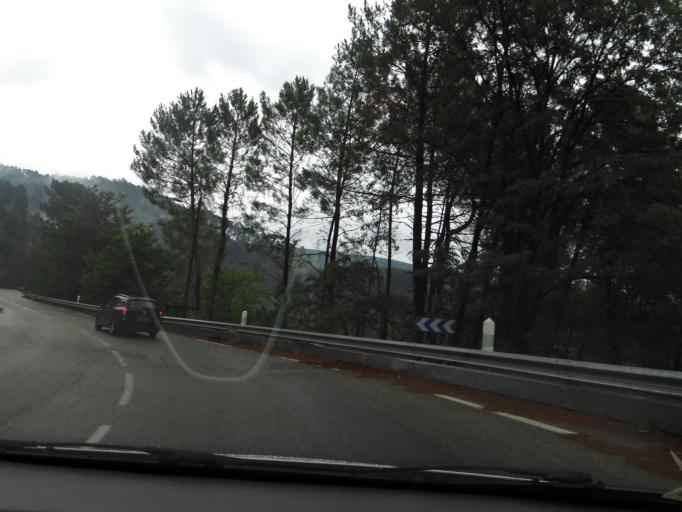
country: FR
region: Languedoc-Roussillon
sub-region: Departement du Gard
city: Branoux-les-Taillades
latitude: 44.2341
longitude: 3.9868
